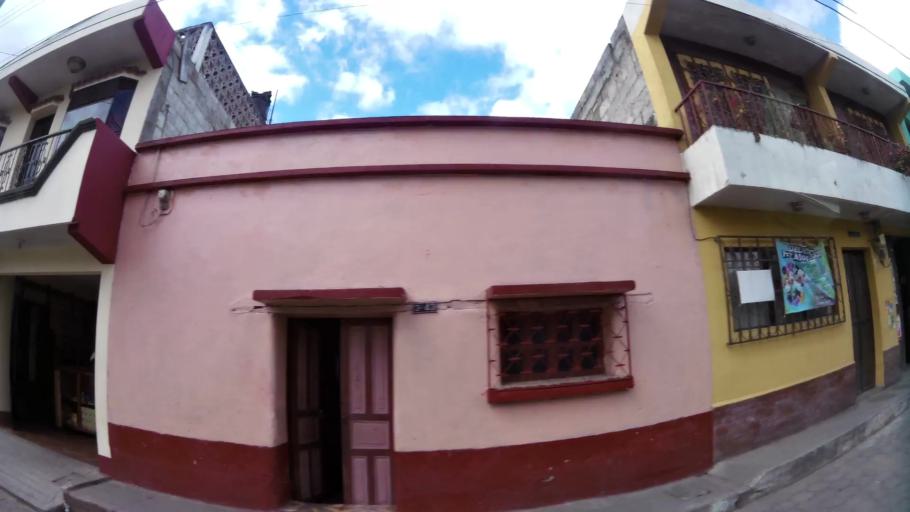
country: GT
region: Quetzaltenango
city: Salcaja
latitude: 14.8770
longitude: -91.4621
